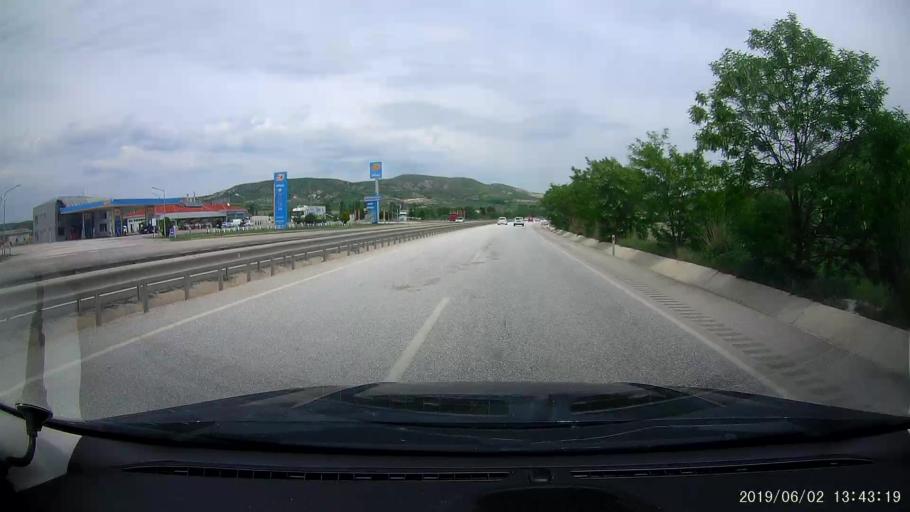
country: TR
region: Cankiri
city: Kursunlu
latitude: 40.8473
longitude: 33.2157
